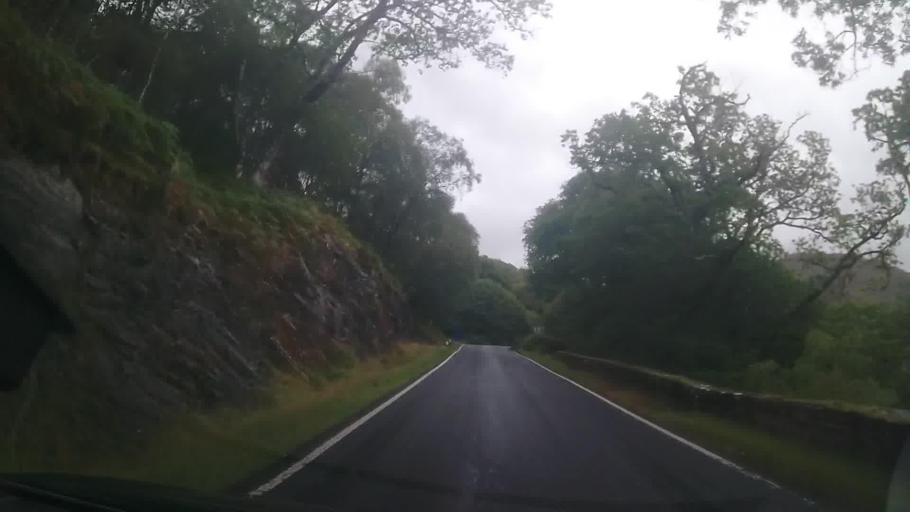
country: GB
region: Scotland
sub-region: Argyll and Bute
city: Isle Of Mull
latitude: 56.6773
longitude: -5.8727
